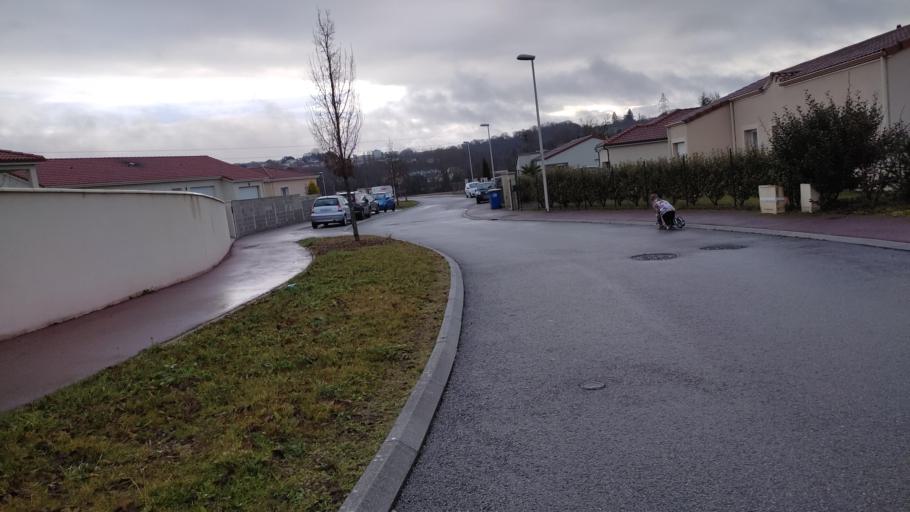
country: FR
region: Limousin
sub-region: Departement de la Haute-Vienne
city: Isle
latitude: 45.8233
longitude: 1.2042
